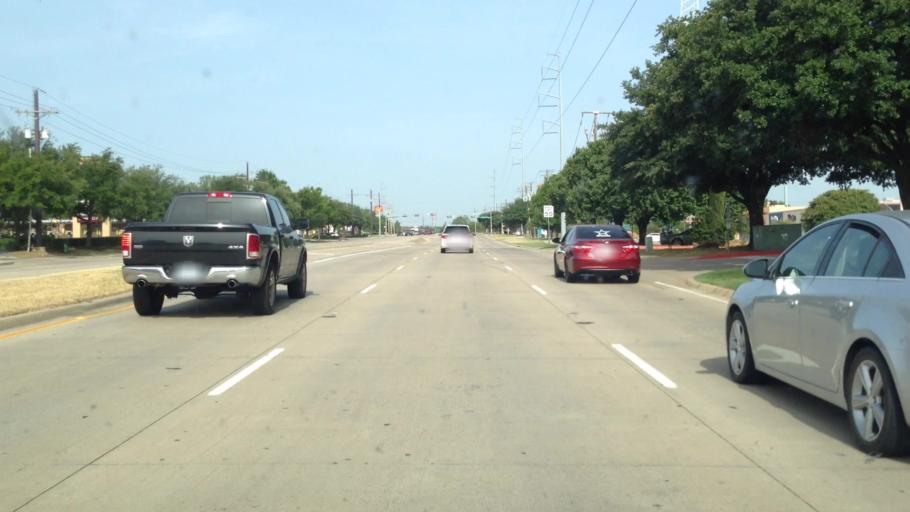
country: US
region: Texas
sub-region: Denton County
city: Lewisville
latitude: 33.0048
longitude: -96.9795
